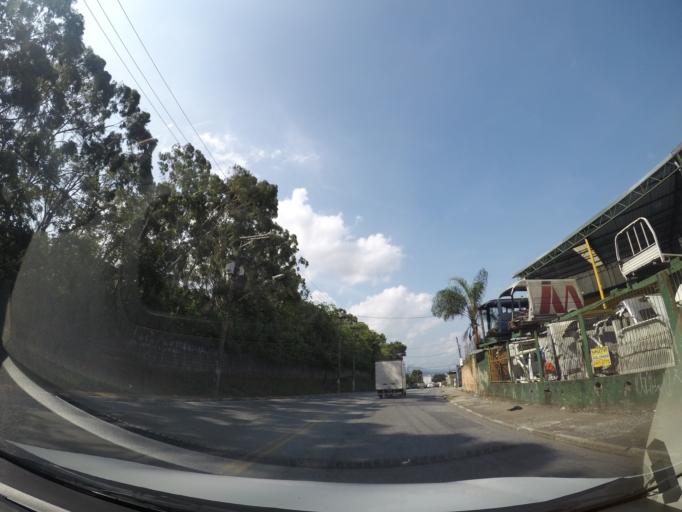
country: BR
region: Sao Paulo
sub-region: Guarulhos
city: Guarulhos
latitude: -23.4461
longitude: -46.4713
